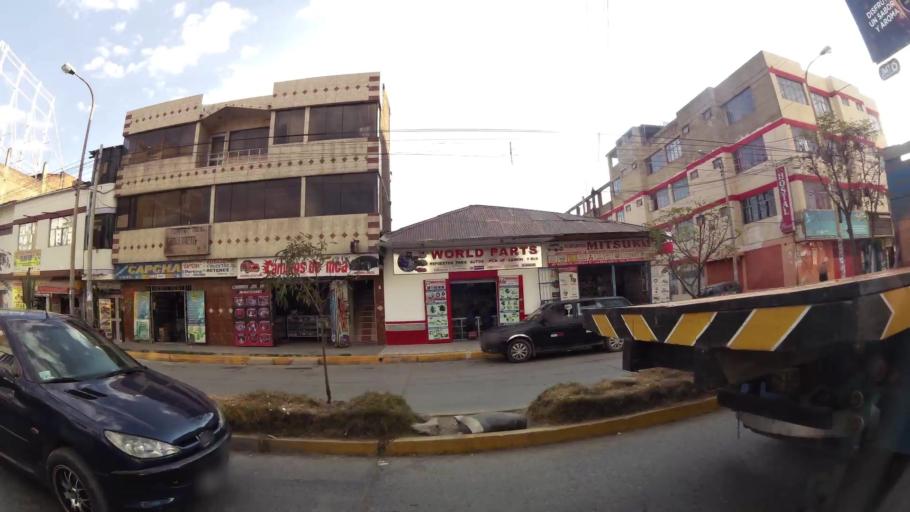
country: PE
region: Junin
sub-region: Provincia de Huancayo
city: El Tambo
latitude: -12.0548
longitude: -75.2190
